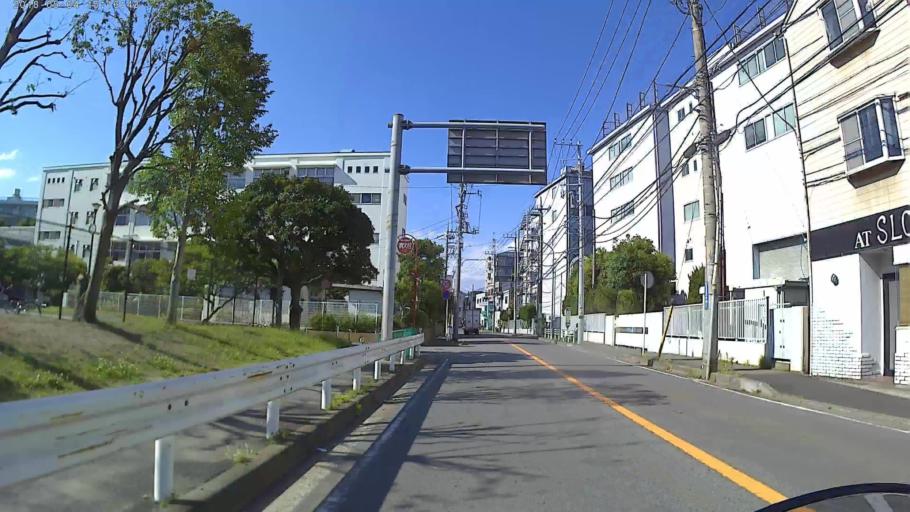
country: JP
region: Kanagawa
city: Yokohama
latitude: 35.5320
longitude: 139.6114
